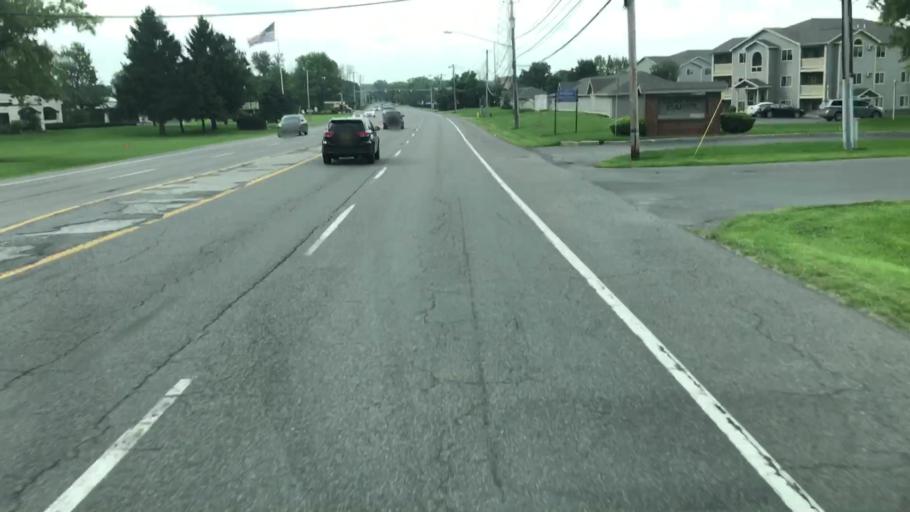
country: US
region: New York
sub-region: Onondaga County
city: Galeville
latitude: 43.1163
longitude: -76.1854
